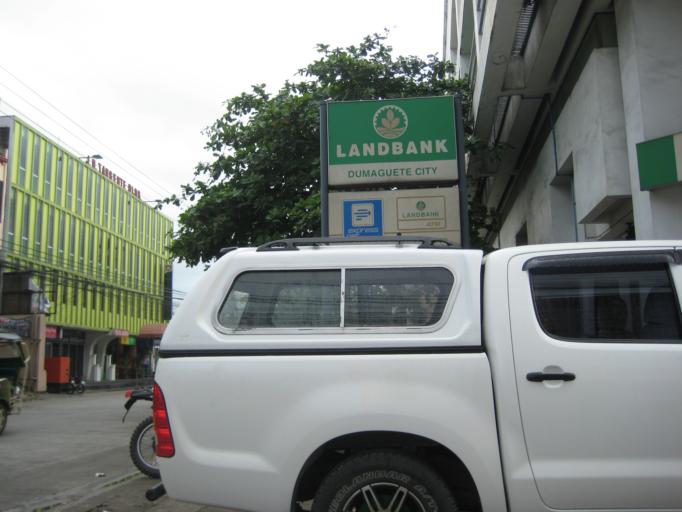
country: PH
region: Central Visayas
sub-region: Province of Negros Oriental
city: Dumaguete
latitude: 9.3092
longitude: 123.3061
